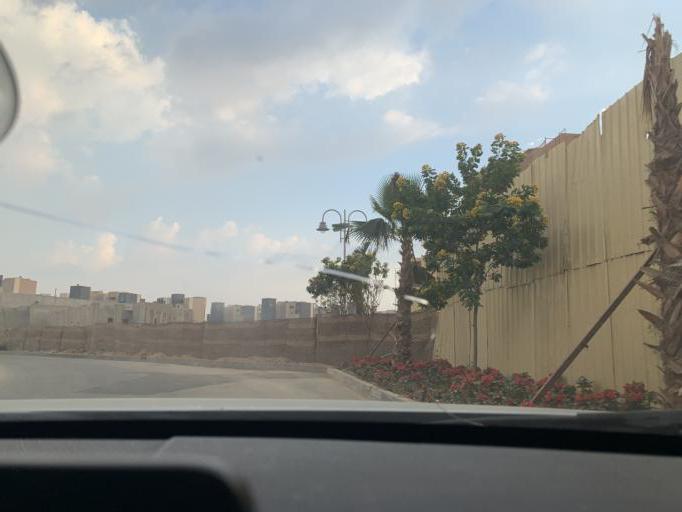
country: EG
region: Muhafazat al Qalyubiyah
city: Al Khankah
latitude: 30.1016
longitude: 31.6507
